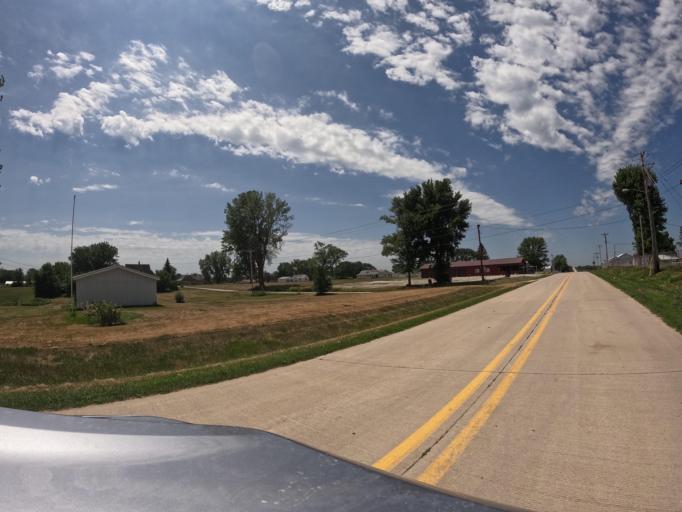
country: US
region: Iowa
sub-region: Keokuk County
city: Sigourney
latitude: 41.4089
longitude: -92.3518
